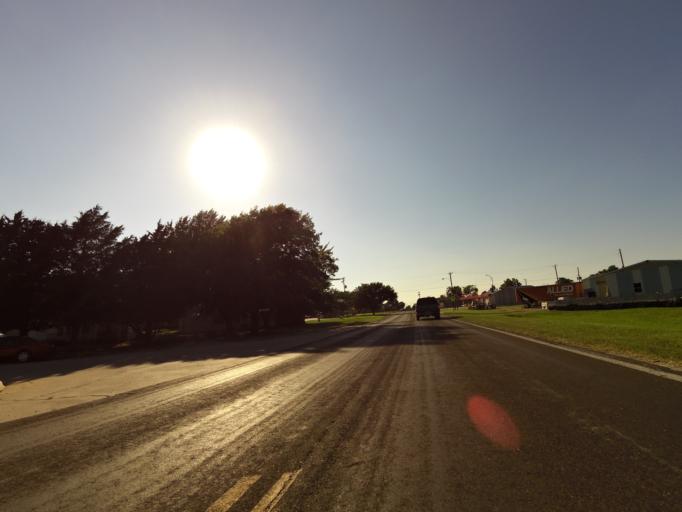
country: US
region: Kansas
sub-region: Harvey County
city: Hesston
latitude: 38.1367
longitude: -97.4285
